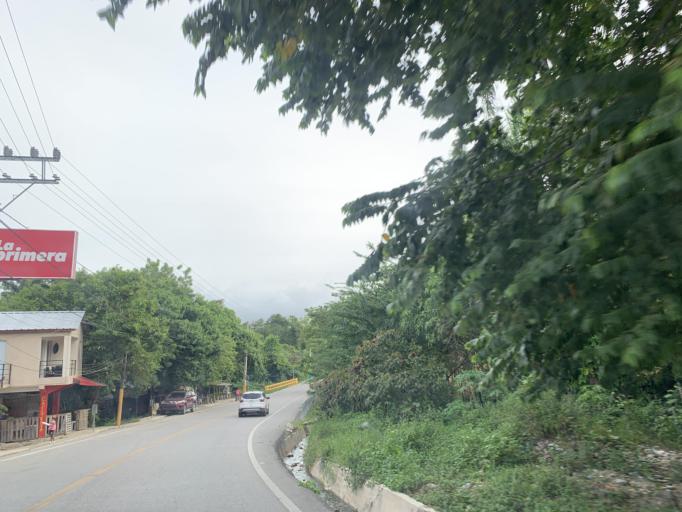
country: DO
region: Puerto Plata
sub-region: Puerto Plata
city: Puerto Plata
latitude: 19.7190
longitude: -70.6195
